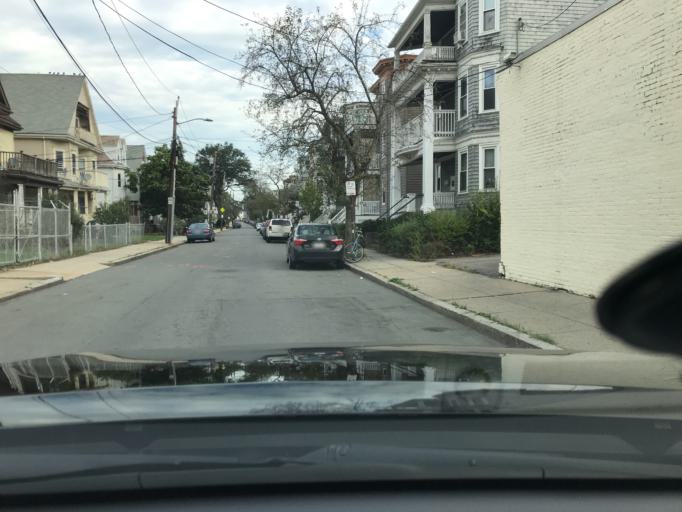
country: US
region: Massachusetts
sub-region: Middlesex County
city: Watertown
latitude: 42.3492
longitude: -71.1631
